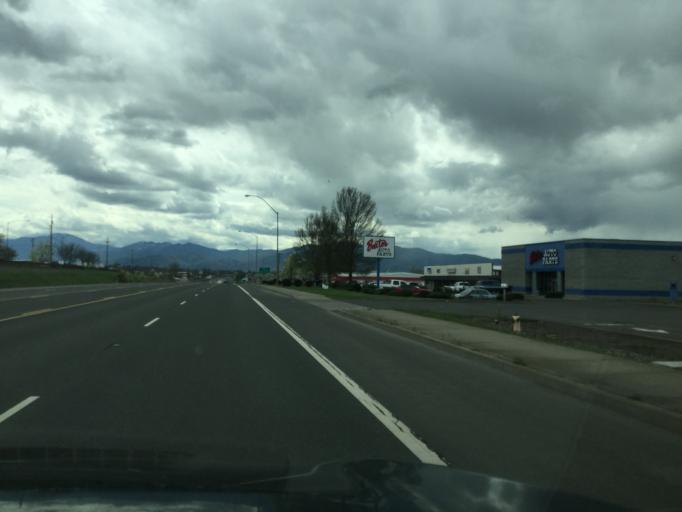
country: US
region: Oregon
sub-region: Jackson County
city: Medford
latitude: 42.3738
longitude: -122.8561
